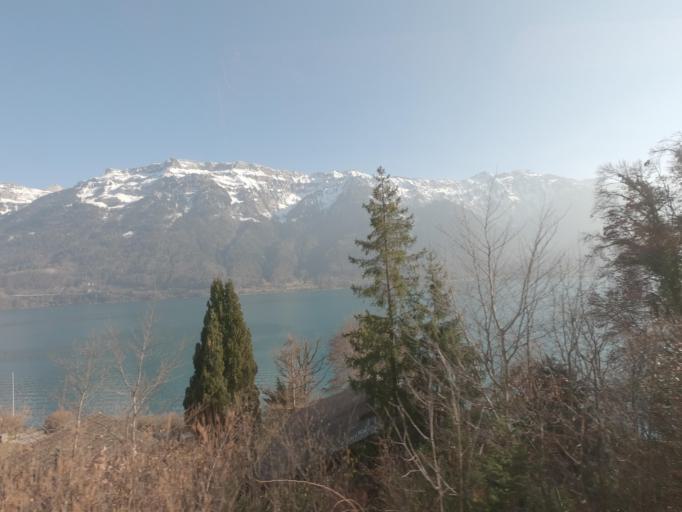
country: CH
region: Bern
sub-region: Interlaken-Oberhasli District
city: Ringgenberg
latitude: 46.7059
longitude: 7.9081
